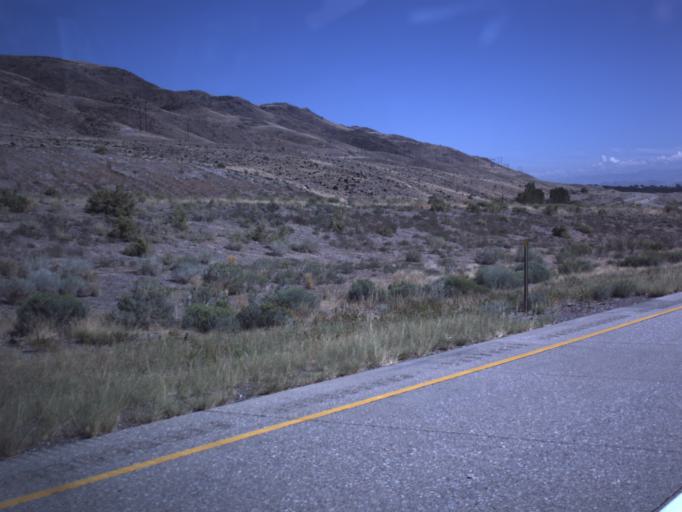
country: US
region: Utah
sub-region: Sevier County
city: Monroe
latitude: 38.6598
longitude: -112.1807
